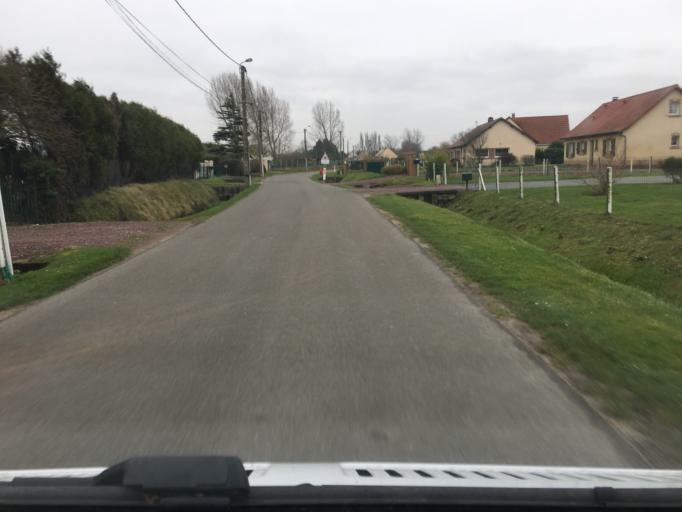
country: FR
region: Picardie
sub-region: Departement de la Somme
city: Pende
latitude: 50.1683
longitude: 1.5514
